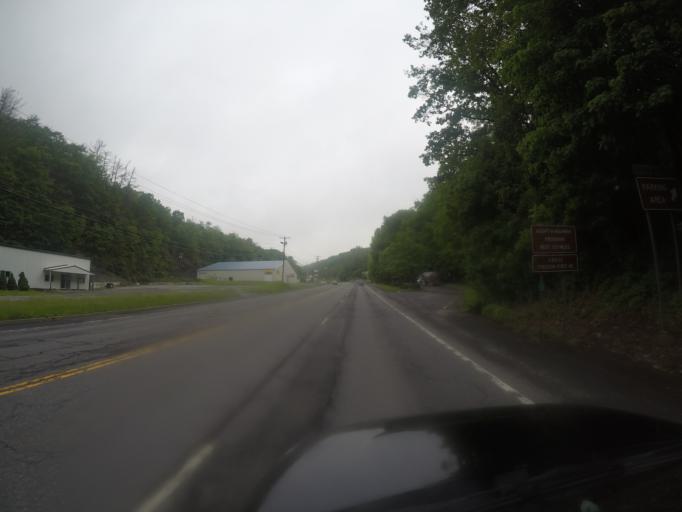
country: US
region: New York
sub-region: Ulster County
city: Hurley
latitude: 41.9675
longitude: -74.0684
